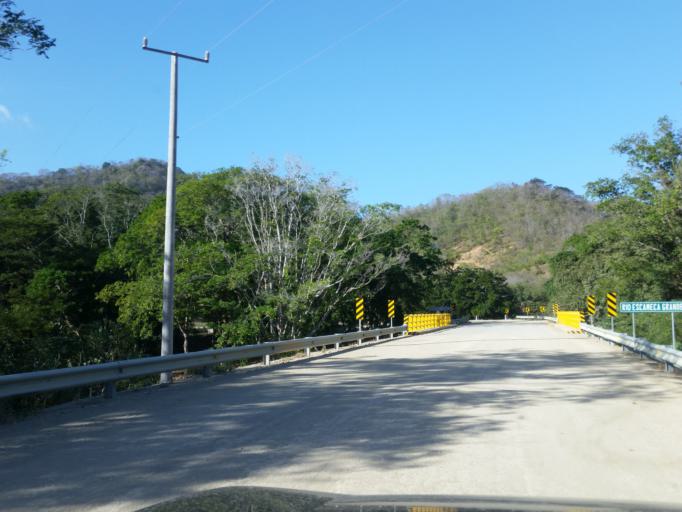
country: NI
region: Rivas
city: San Juan del Sur
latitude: 11.1748
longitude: -85.8007
